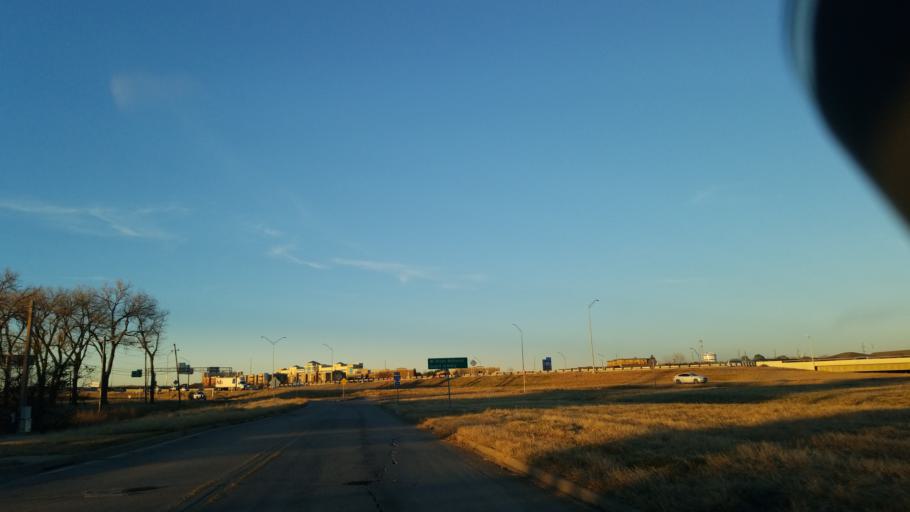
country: US
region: Texas
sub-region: Denton County
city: Denton
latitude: 33.2094
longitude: -97.1661
